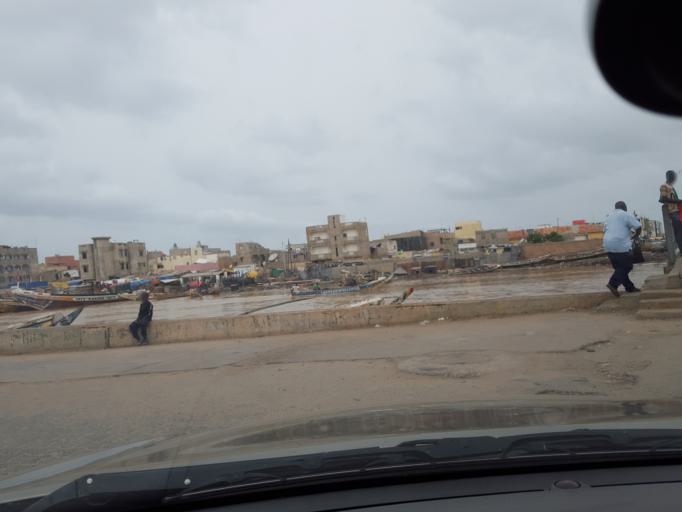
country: SN
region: Saint-Louis
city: Saint-Louis
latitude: 16.0260
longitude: -16.5061
